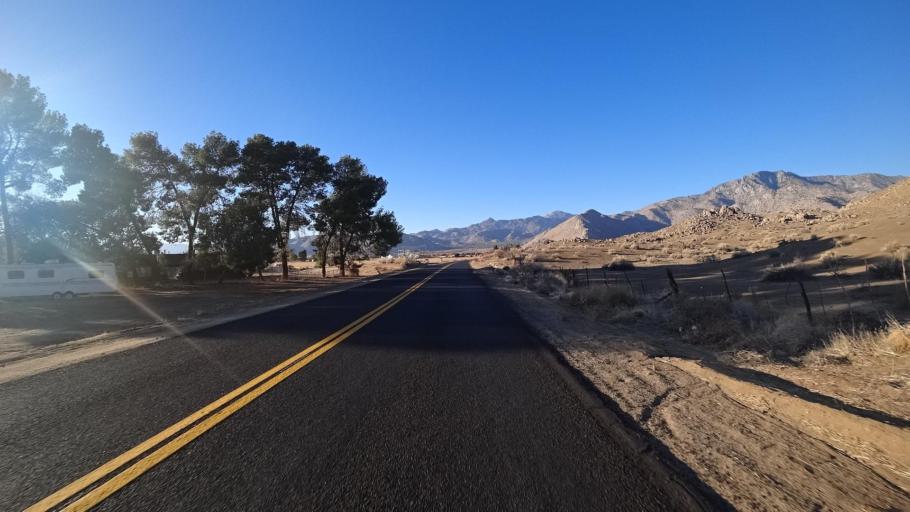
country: US
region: California
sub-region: Kern County
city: Weldon
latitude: 35.6637
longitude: -118.2583
